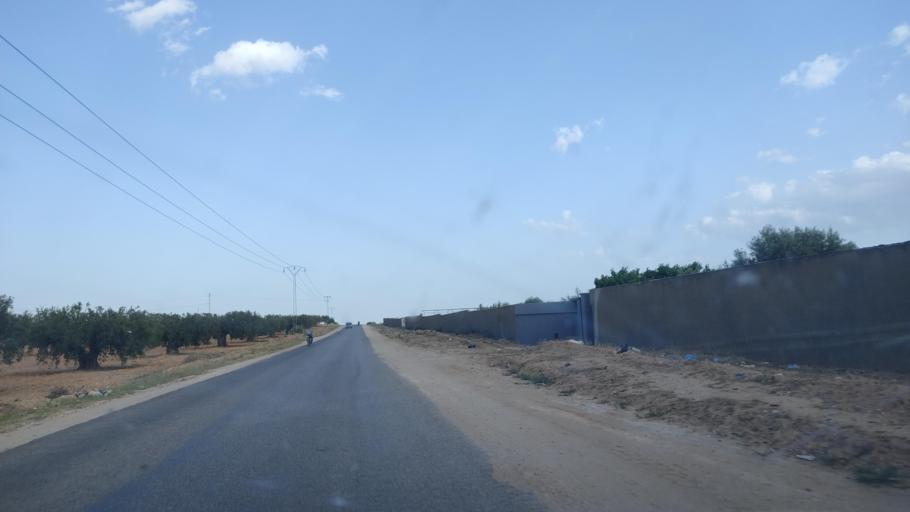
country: TN
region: Safaqis
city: Sfax
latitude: 34.8419
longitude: 10.6223
